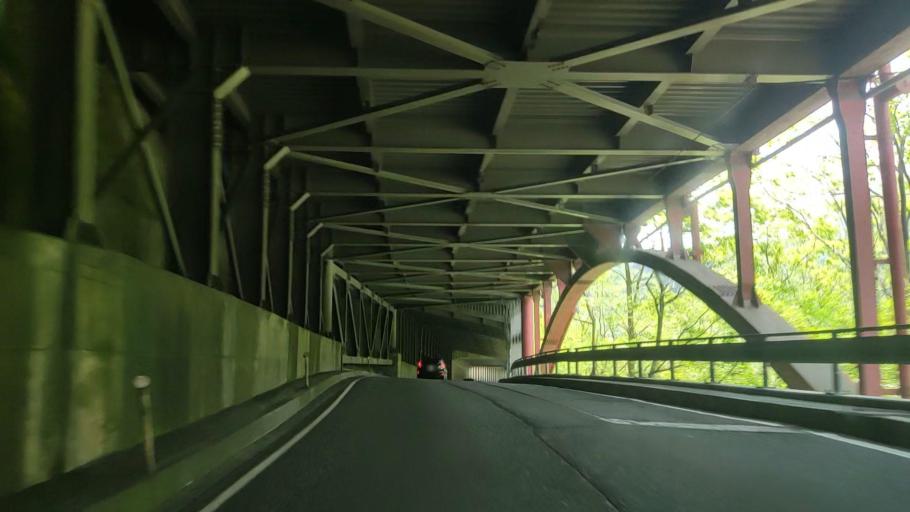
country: JP
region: Niigata
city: Itoigawa
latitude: 36.9547
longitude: 137.8595
